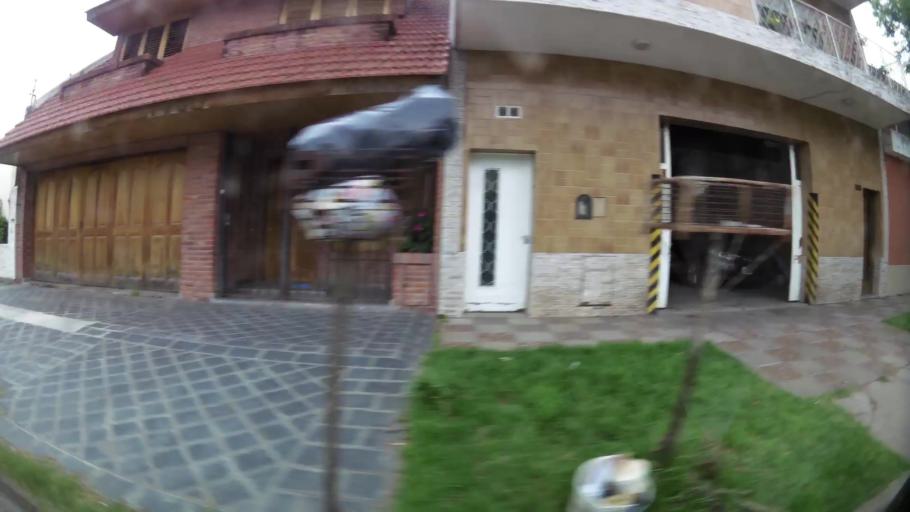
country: AR
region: Buenos Aires
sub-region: Partido de Zarate
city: Zarate
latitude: -34.0971
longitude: -59.0339
